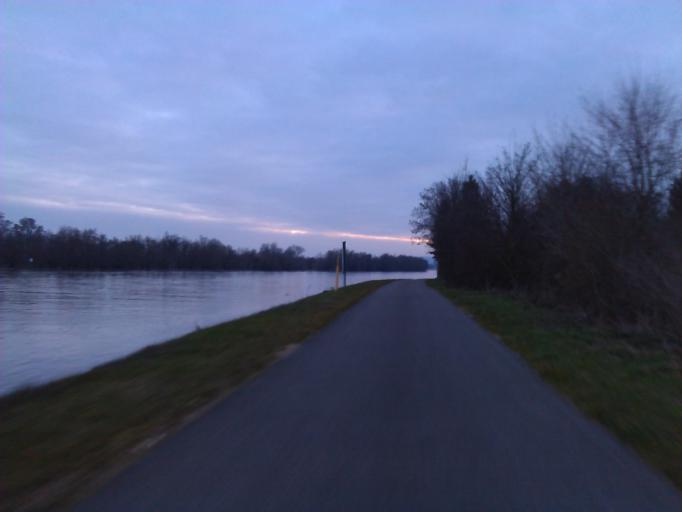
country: DE
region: Hesse
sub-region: Regierungsbezirk Darmstadt
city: Kiedrich
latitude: 50.0127
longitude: 8.0681
